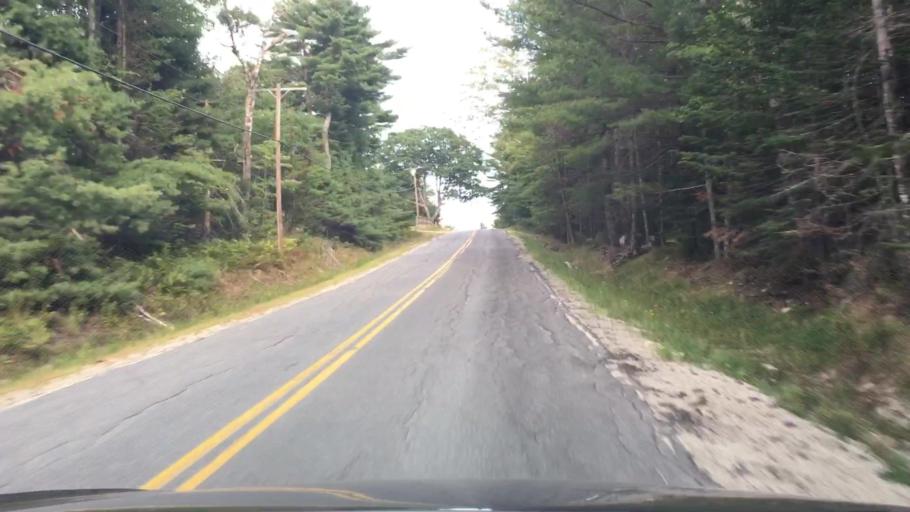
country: US
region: Maine
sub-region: Hancock County
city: Surry
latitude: 44.5004
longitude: -68.5684
